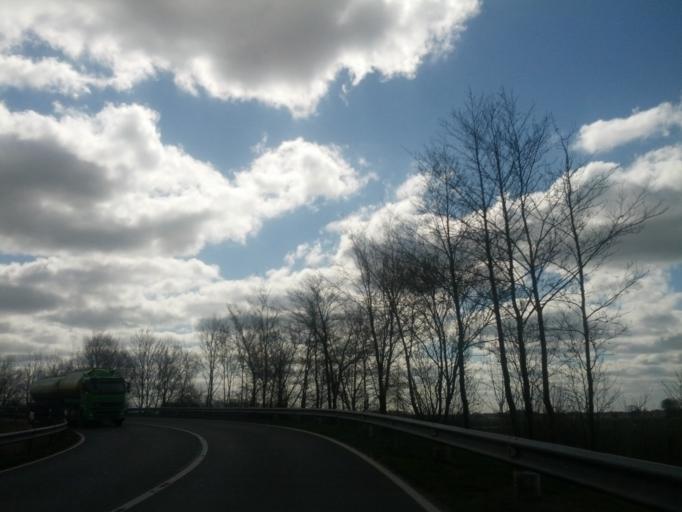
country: DE
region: Lower Saxony
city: Wittmund
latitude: 53.5760
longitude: 7.7983
